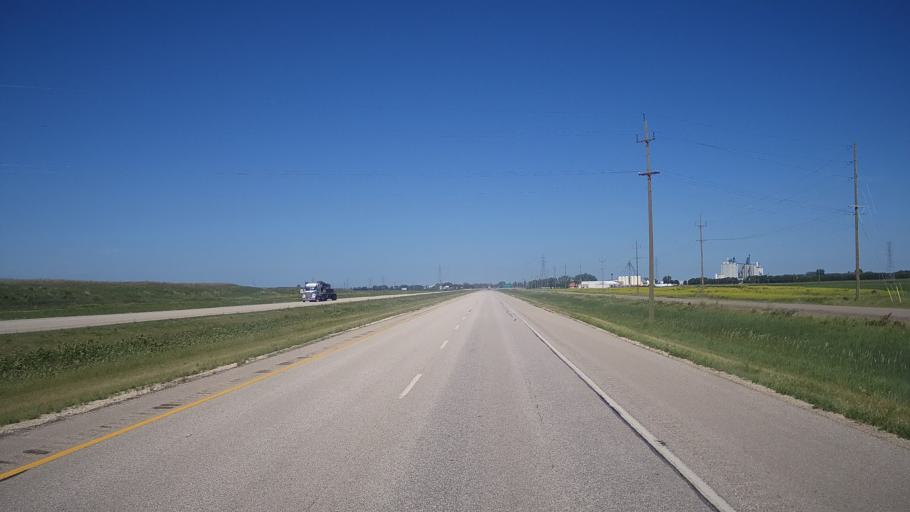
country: CA
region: Manitoba
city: Portage la Prairie
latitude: 49.9570
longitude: -98.3343
